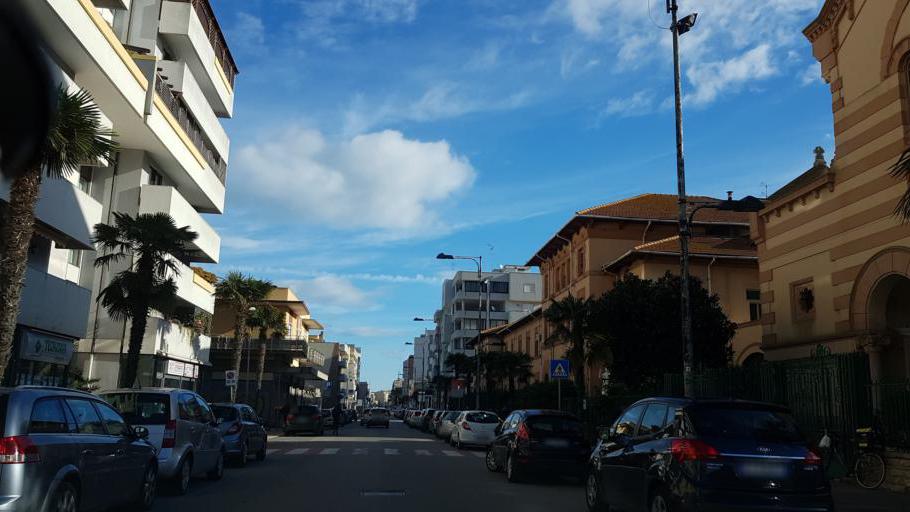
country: IT
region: Apulia
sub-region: Provincia di Brindisi
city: Brindisi
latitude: 40.6304
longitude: 17.9273
